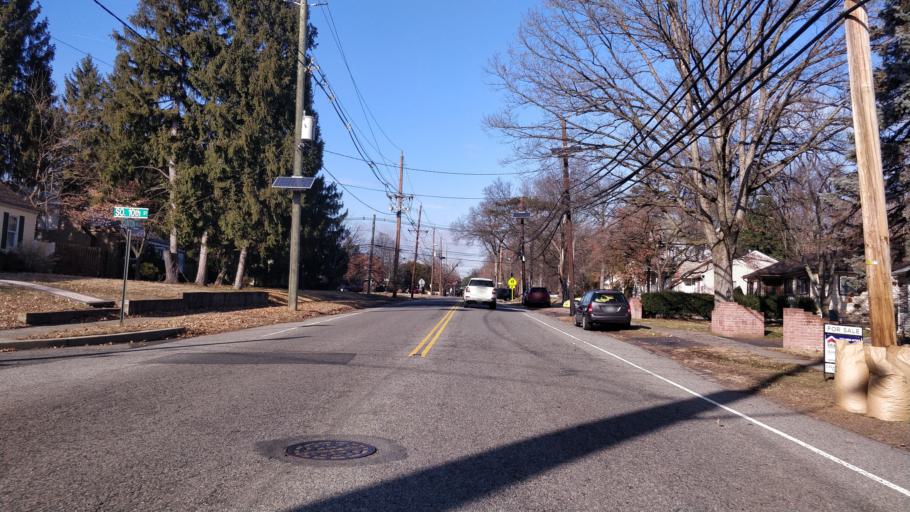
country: US
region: New Jersey
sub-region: Middlesex County
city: South Plainfield
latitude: 40.5913
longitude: -74.4333
